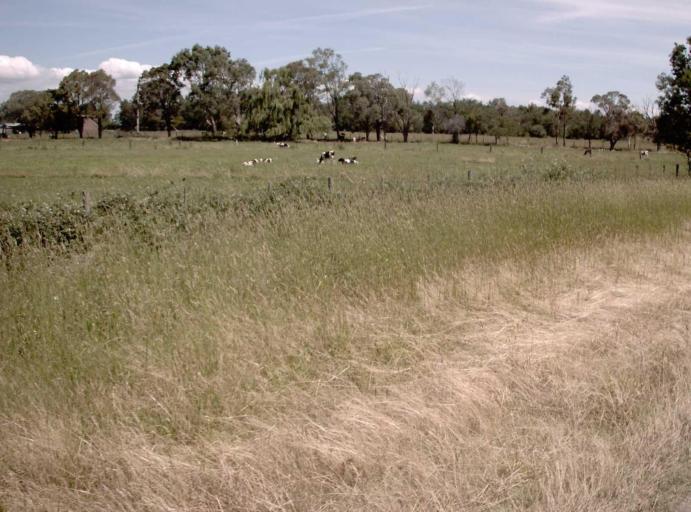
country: AU
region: Victoria
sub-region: Wellington
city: Heyfield
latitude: -38.0065
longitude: 146.8818
